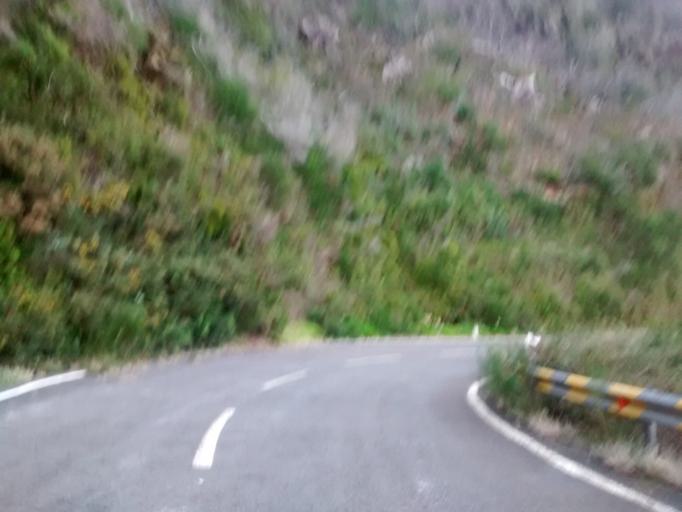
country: PT
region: Madeira
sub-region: Sao Vicente
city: Sao Vicente
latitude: 32.7443
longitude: -17.0436
